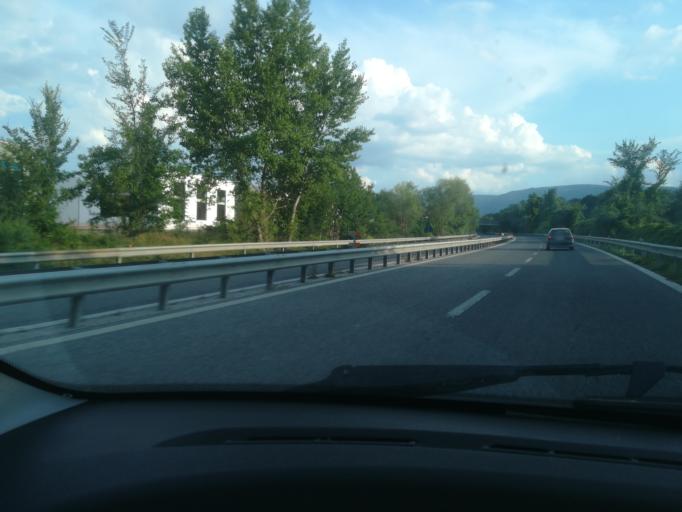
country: IT
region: The Marches
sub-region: Provincia di Macerata
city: Belforte del Chienti
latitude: 43.1803
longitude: 13.2506
